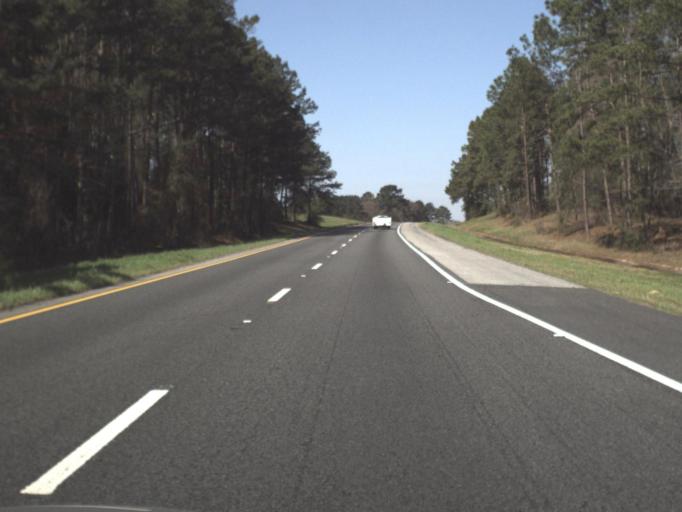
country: US
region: Florida
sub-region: Jackson County
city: Sneads
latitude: 30.6396
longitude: -84.9914
